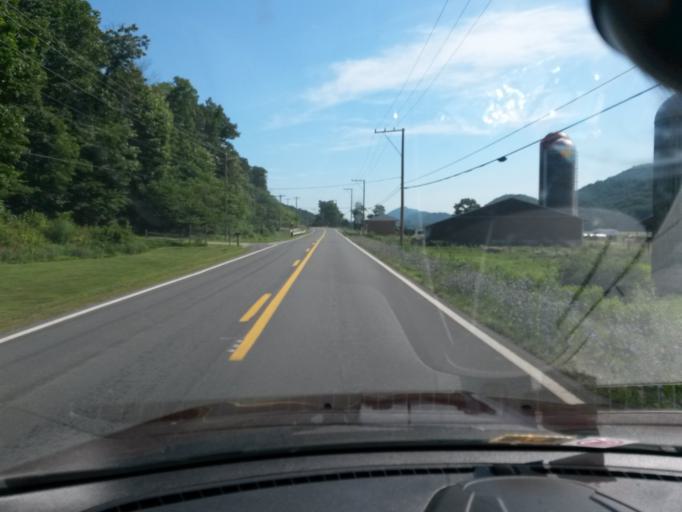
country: US
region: West Virginia
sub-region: Hardy County
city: Moorefield
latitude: 39.0174
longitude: -78.7637
